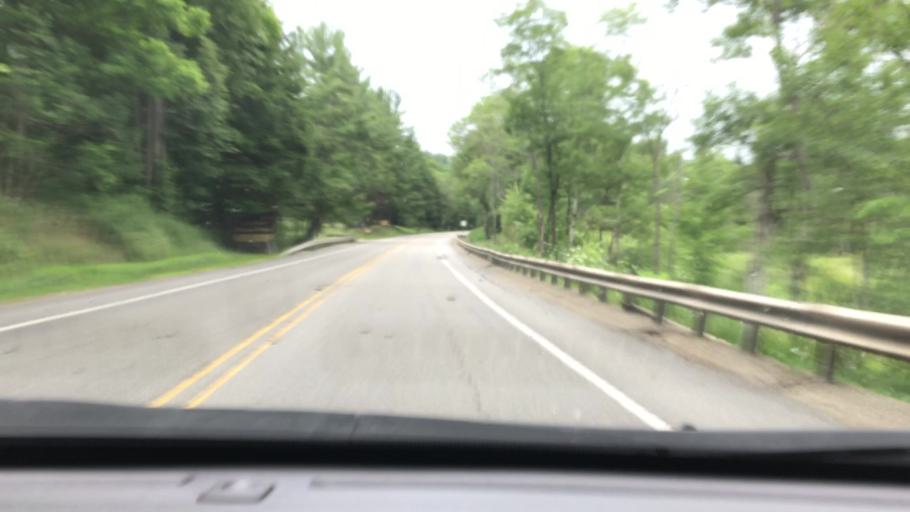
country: US
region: Pennsylvania
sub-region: McKean County
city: Bradford
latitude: 41.8588
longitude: -78.6729
